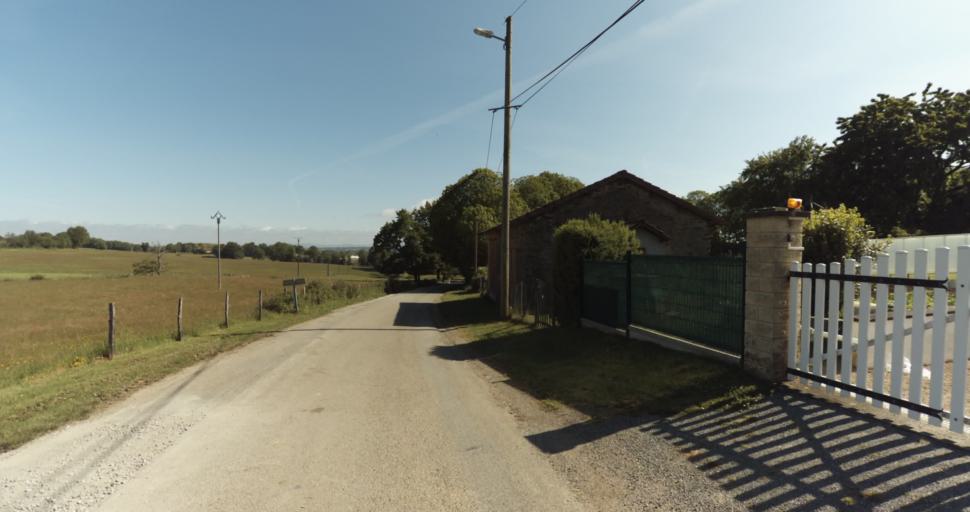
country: FR
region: Limousin
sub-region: Departement de la Haute-Vienne
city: Solignac
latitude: 45.7205
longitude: 1.2676
